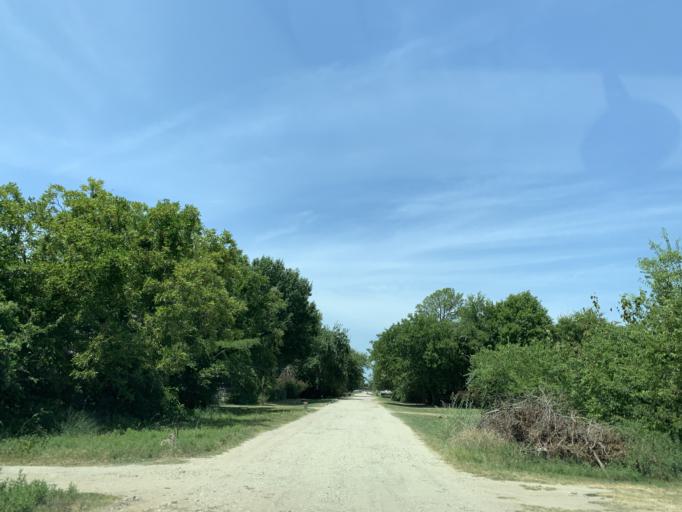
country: US
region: Texas
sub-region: Dallas County
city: Cedar Hill
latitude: 32.6411
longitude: -97.0251
